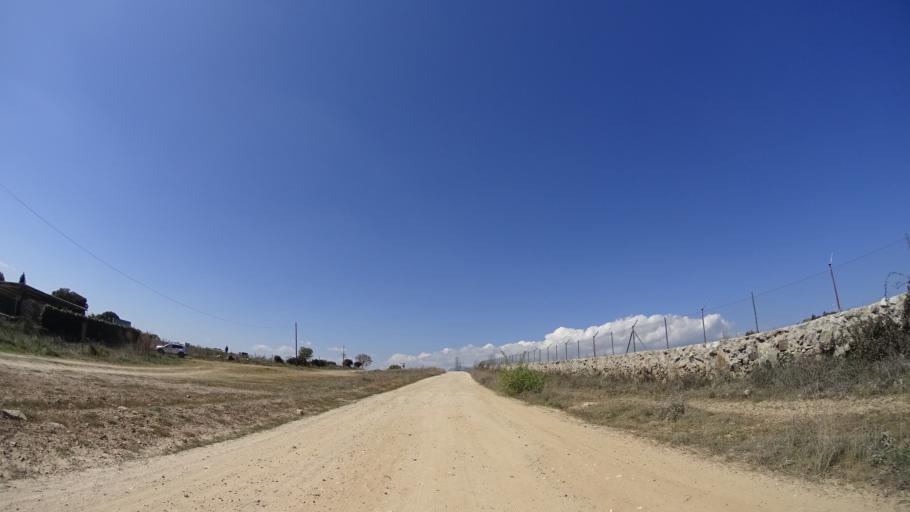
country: ES
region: Madrid
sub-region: Provincia de Madrid
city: Colmenar Viejo
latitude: 40.6865
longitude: -3.7613
